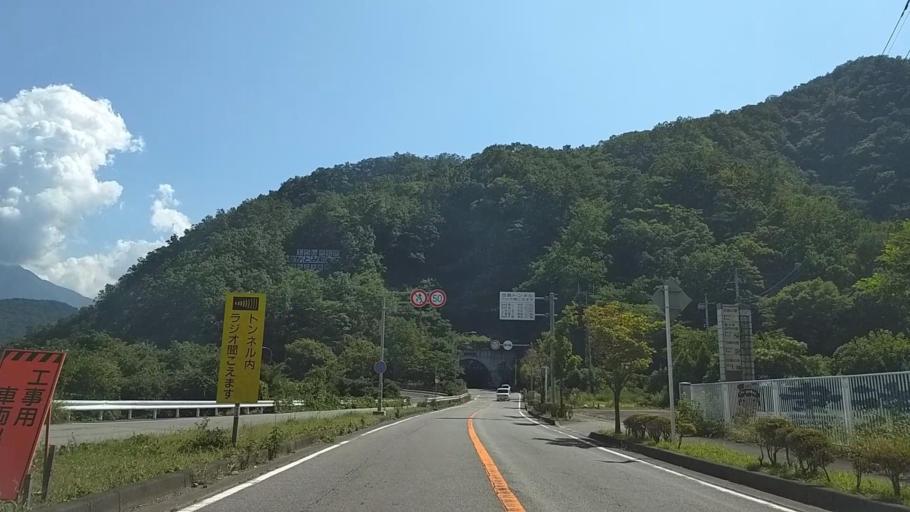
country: JP
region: Yamanashi
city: Ryuo
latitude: 35.4998
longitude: 138.4461
